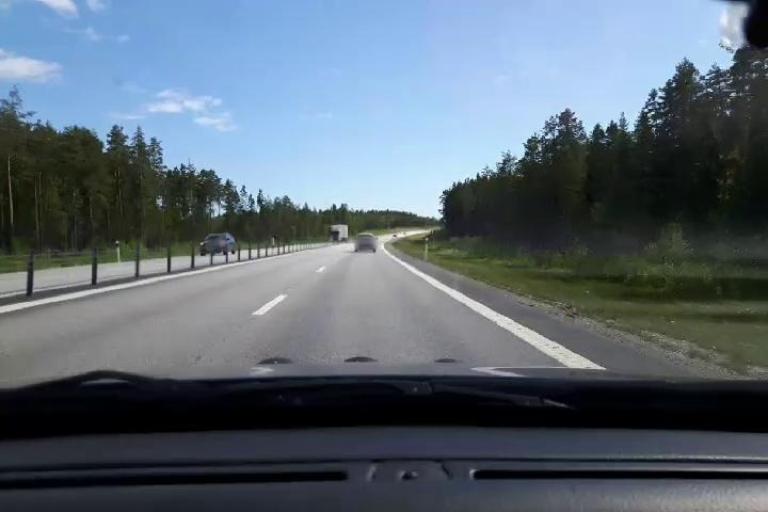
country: SE
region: Gaevleborg
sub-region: Hudiksvalls Kommun
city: Hudiksvall
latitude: 61.7004
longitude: 17.0550
